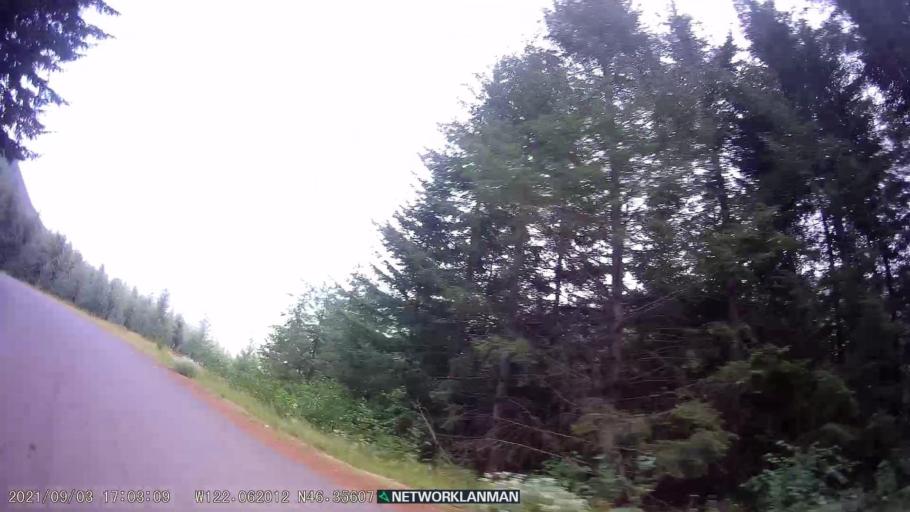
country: US
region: Washington
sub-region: Lewis County
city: Morton
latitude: 46.3563
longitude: -122.0618
